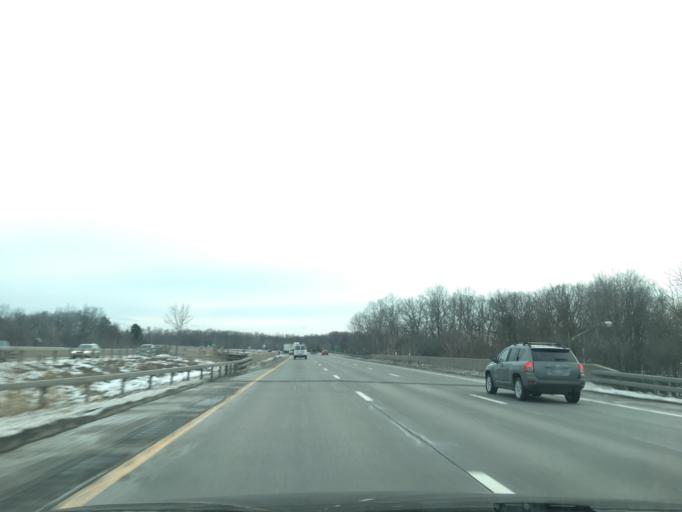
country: US
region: New York
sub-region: Monroe County
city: Fairport
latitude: 43.0425
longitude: -77.4626
